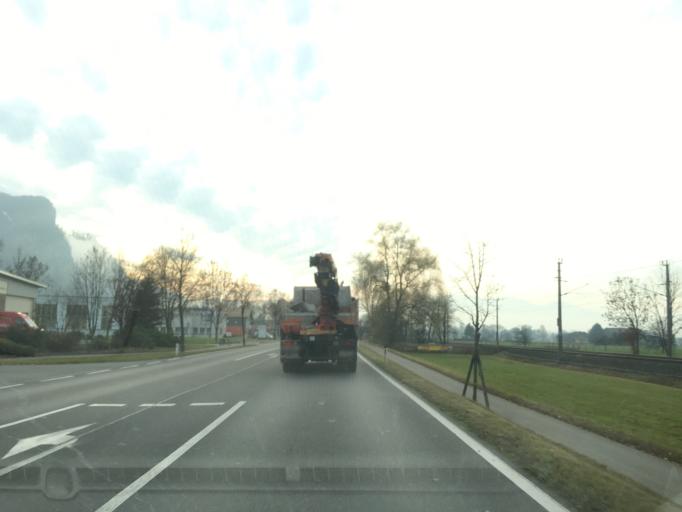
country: AT
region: Vorarlberg
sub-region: Politischer Bezirk Dornbirn
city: Hohenems
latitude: 47.3797
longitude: 9.7040
